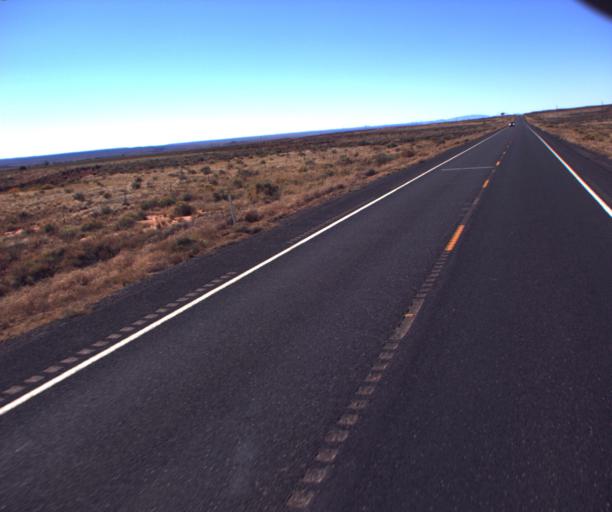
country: US
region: Arizona
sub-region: Coconino County
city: Fredonia
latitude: 36.9270
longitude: -112.5654
